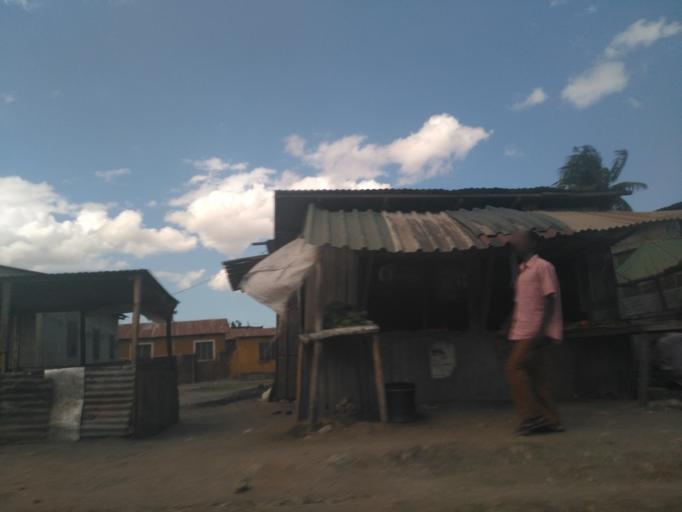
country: TZ
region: Dar es Salaam
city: Dar es Salaam
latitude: -6.8743
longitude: 39.2403
